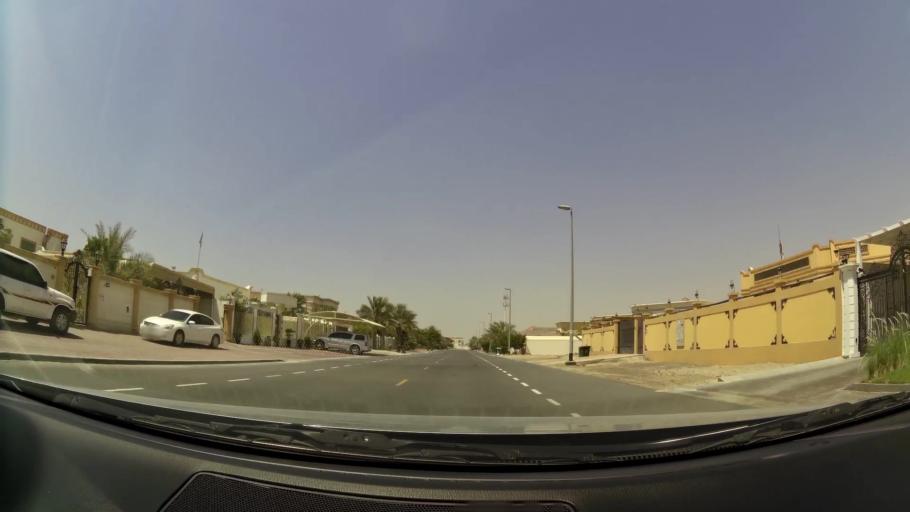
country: AE
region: Dubai
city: Dubai
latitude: 25.1057
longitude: 55.2177
